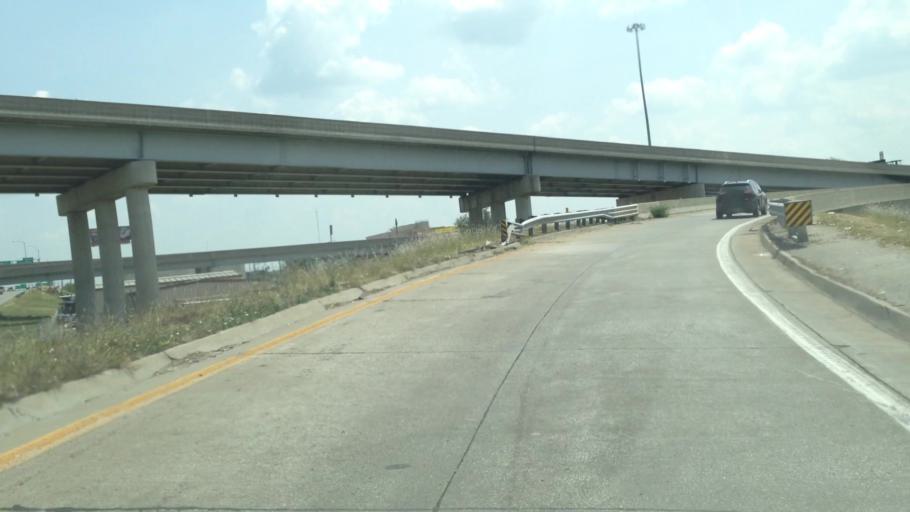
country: US
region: Missouri
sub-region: Jackson County
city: Kansas City
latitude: 39.0959
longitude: -94.5759
